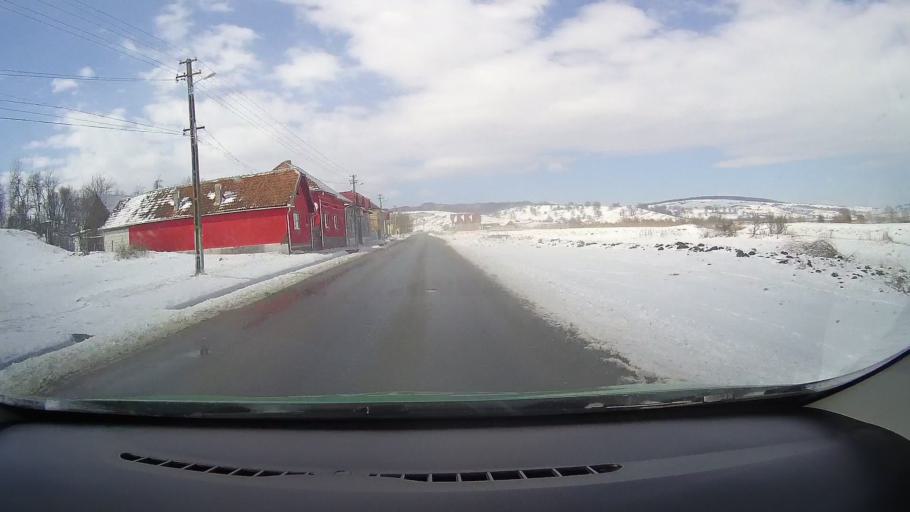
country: RO
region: Sibiu
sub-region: Comuna Altina
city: Altina
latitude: 45.9381
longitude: 24.4583
